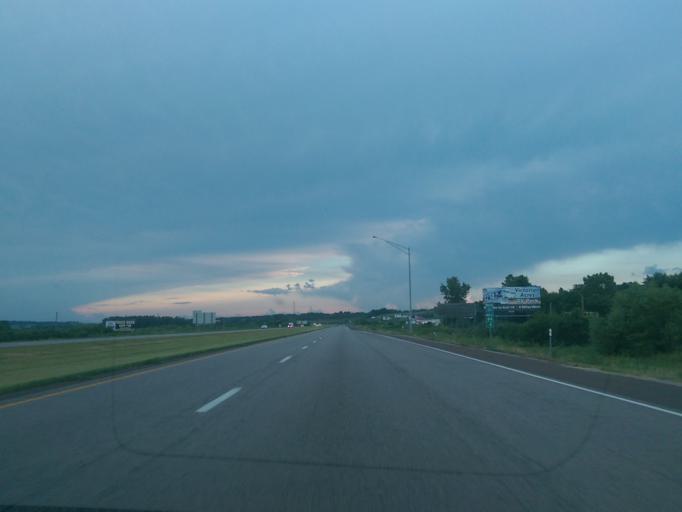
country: US
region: Missouri
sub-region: Holt County
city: Mound City
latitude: 40.1355
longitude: -95.2388
